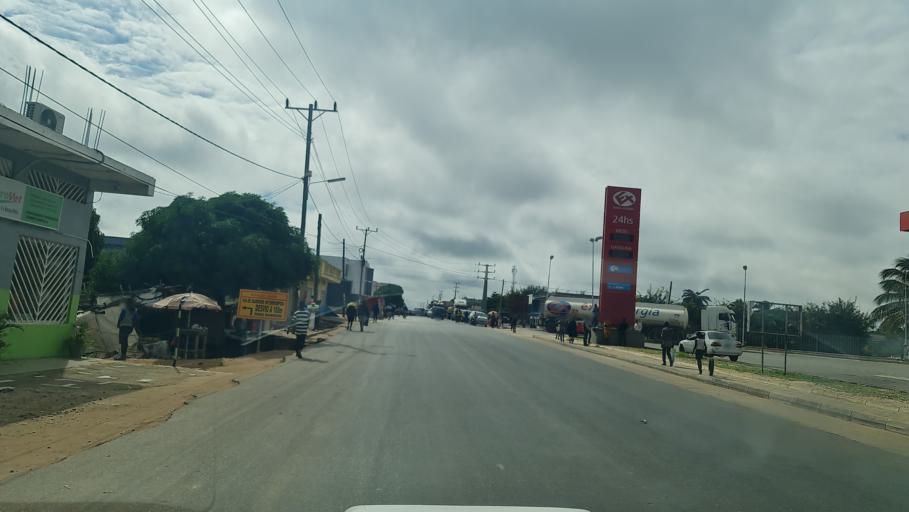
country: MZ
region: Nampula
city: Nampula
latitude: -15.1120
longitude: 39.2266
